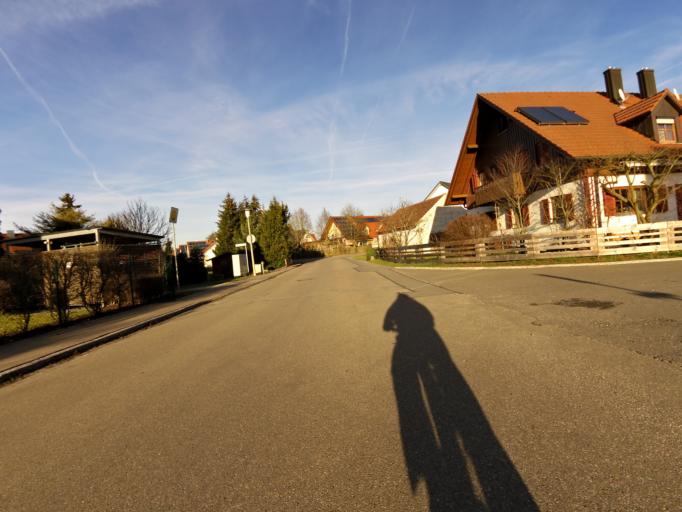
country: DE
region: Bavaria
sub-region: Lower Bavaria
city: Eching
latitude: 48.4945
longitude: 12.0293
